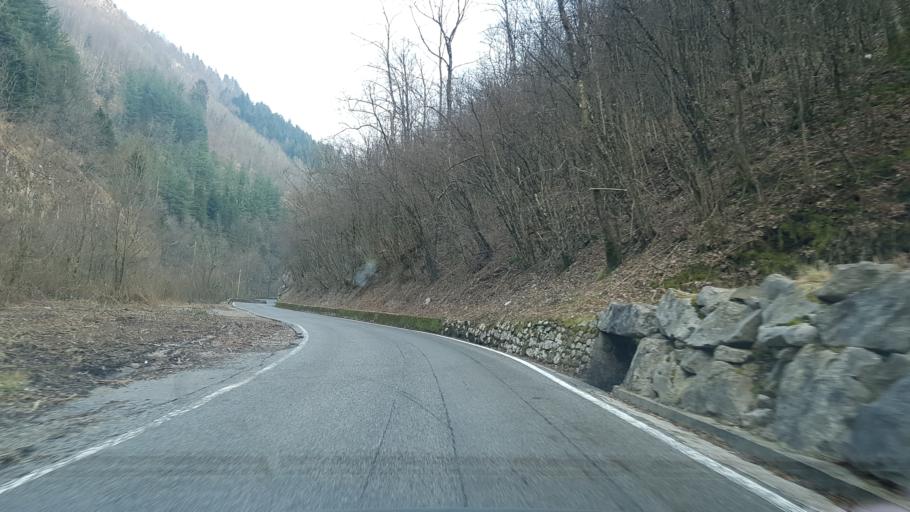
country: IT
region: Friuli Venezia Giulia
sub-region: Provincia di Udine
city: Taipana
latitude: 46.2495
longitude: 13.3236
